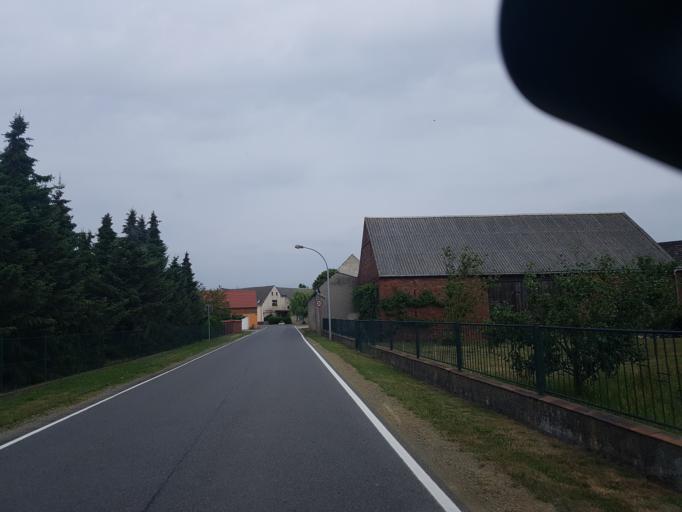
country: DE
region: Brandenburg
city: Schonewalde
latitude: 51.7018
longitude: 13.6032
